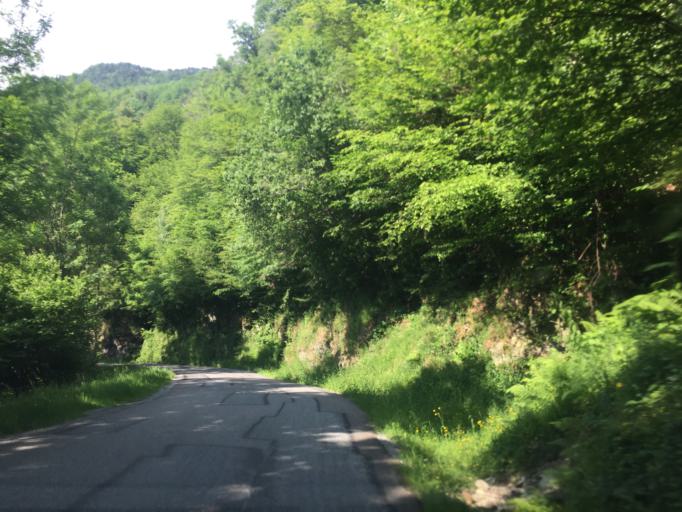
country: FR
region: Rhone-Alpes
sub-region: Departement de la Savoie
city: Aiton
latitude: 45.5312
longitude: 6.3301
